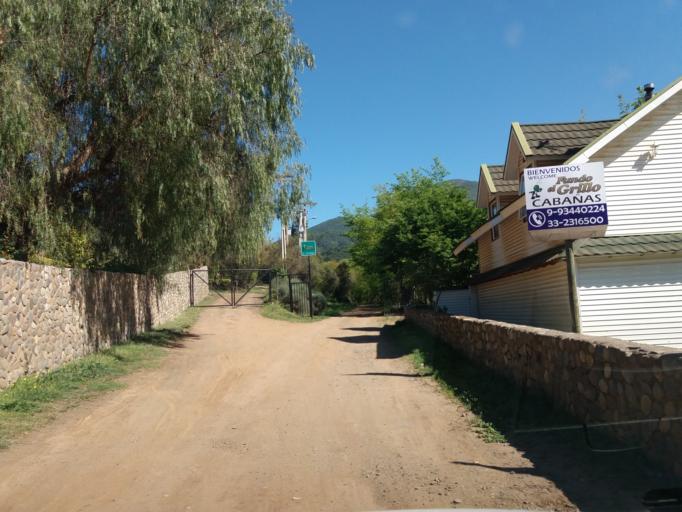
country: CL
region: Valparaiso
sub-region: Provincia de Quillota
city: Quillota
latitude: -32.8535
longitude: -71.2946
